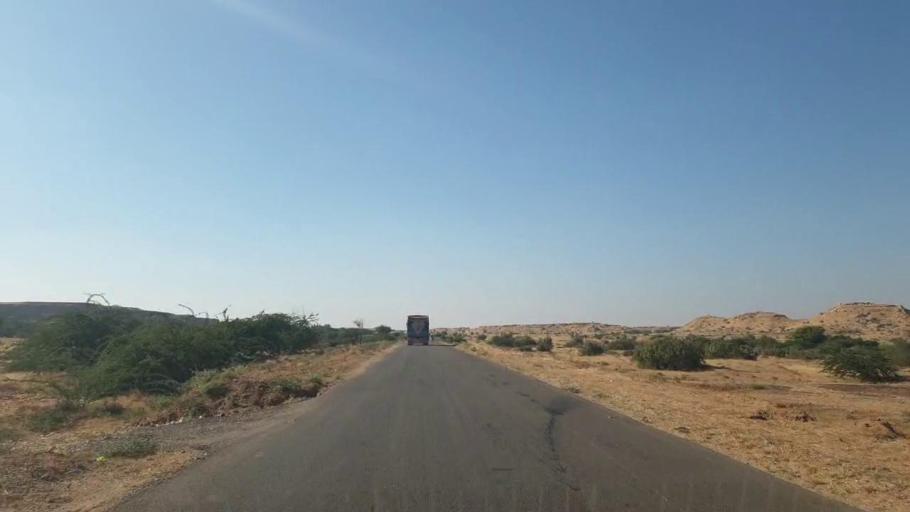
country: PK
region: Sindh
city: Gharo
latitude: 25.2212
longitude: 67.6180
